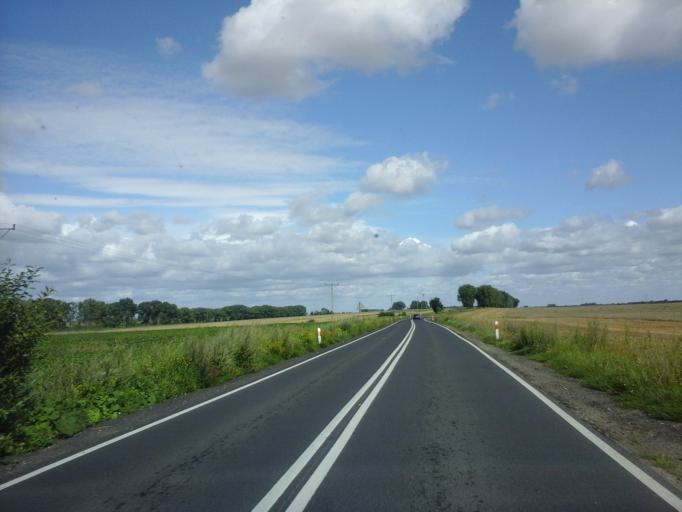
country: PL
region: West Pomeranian Voivodeship
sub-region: Powiat stargardzki
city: Stargard Szczecinski
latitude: 53.2449
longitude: 15.1055
